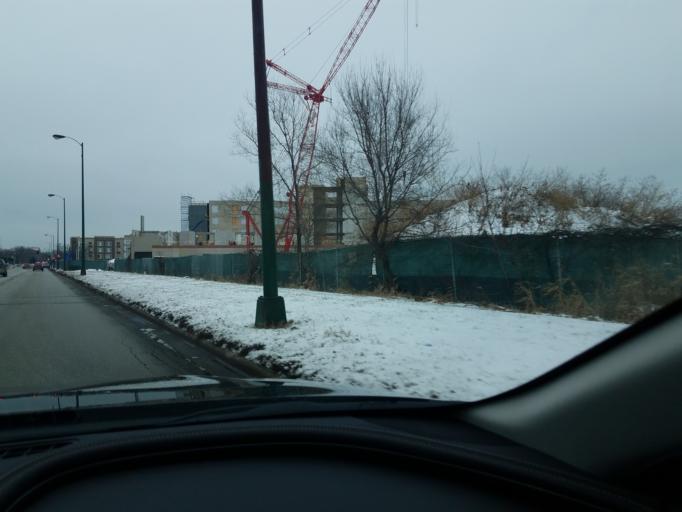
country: US
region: Illinois
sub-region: Cook County
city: Harwood Heights
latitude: 41.9575
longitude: -87.7991
